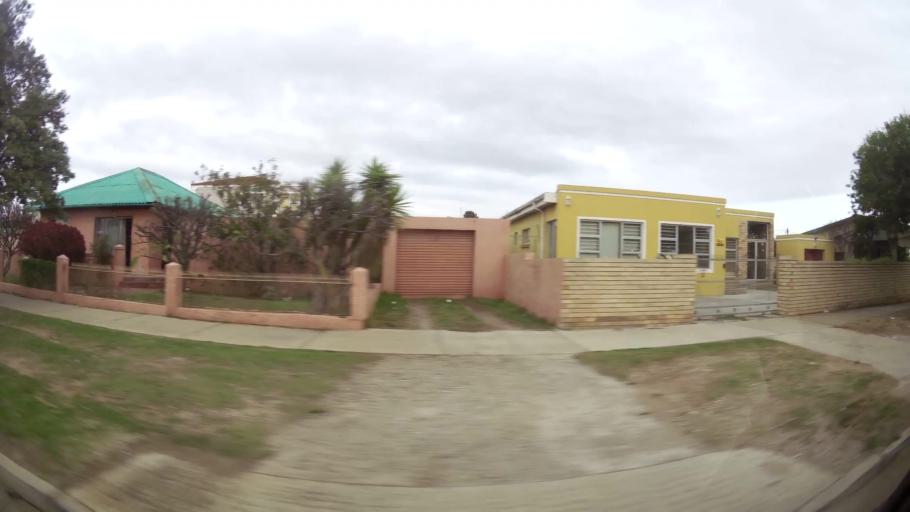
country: ZA
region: Eastern Cape
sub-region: Nelson Mandela Bay Metropolitan Municipality
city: Port Elizabeth
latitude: -33.9172
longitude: 25.5635
